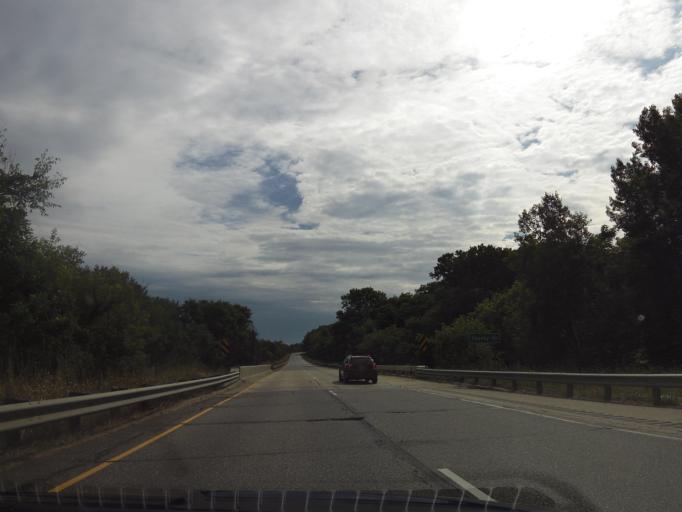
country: US
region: Wisconsin
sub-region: La Crosse County
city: Brice Prairie
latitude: 43.9209
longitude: -91.3922
